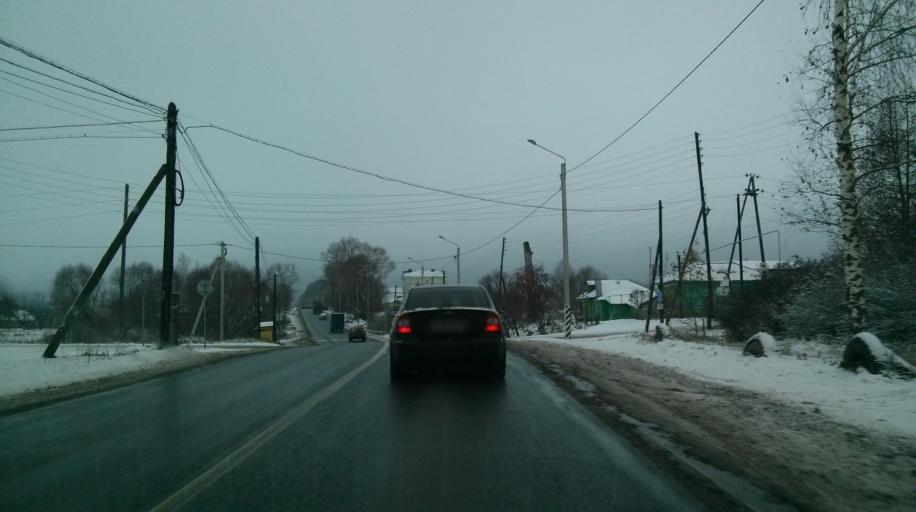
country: RU
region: Nizjnij Novgorod
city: Vorsma
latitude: 56.0377
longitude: 43.3700
